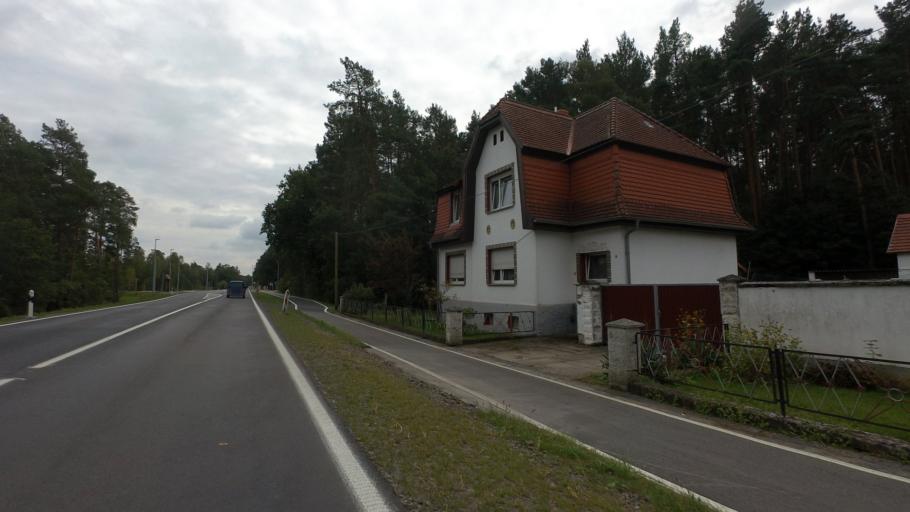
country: DE
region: Brandenburg
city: Baruth
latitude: 52.0326
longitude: 13.5270
